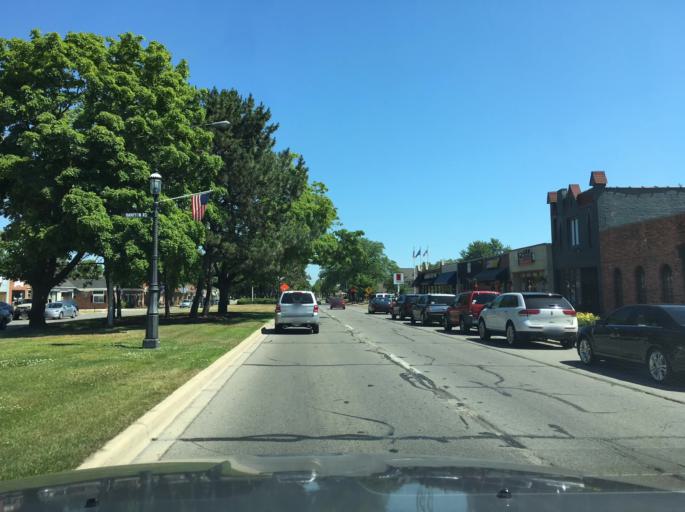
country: US
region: Michigan
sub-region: Wayne County
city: Grosse Pointe Woods
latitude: 42.4478
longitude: -82.9057
